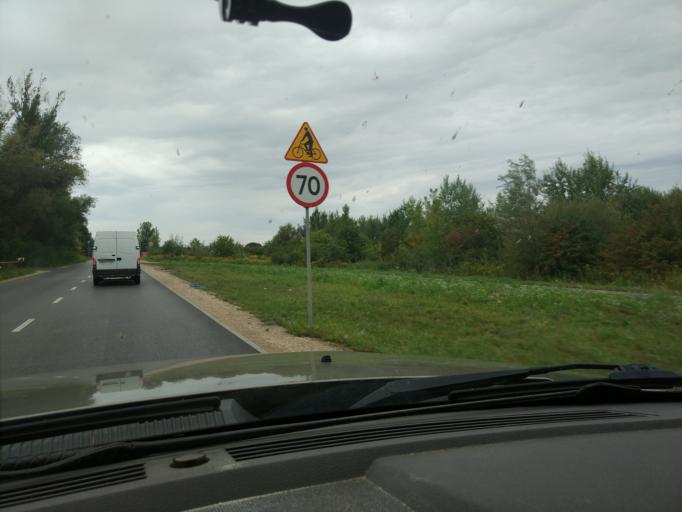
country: PL
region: Masovian Voivodeship
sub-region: Powiat pruszkowski
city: Brwinow
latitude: 52.1739
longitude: 20.7502
